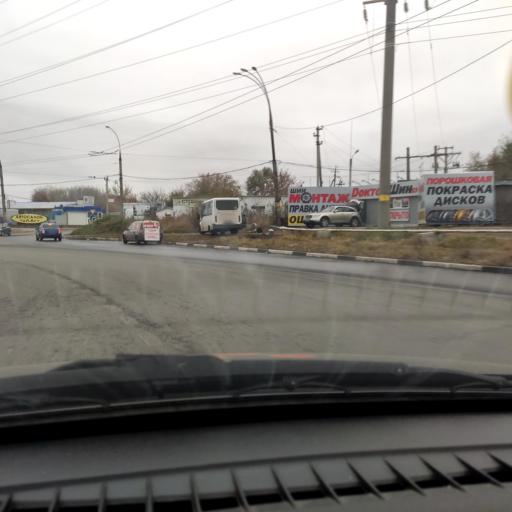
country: RU
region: Samara
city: Tol'yatti
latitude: 53.5311
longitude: 49.2613
